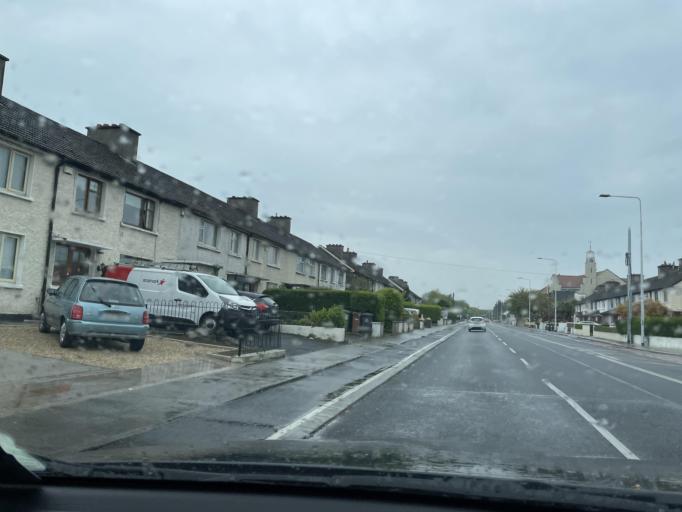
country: IE
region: Leinster
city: Dundrum
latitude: 53.2941
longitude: -6.2587
